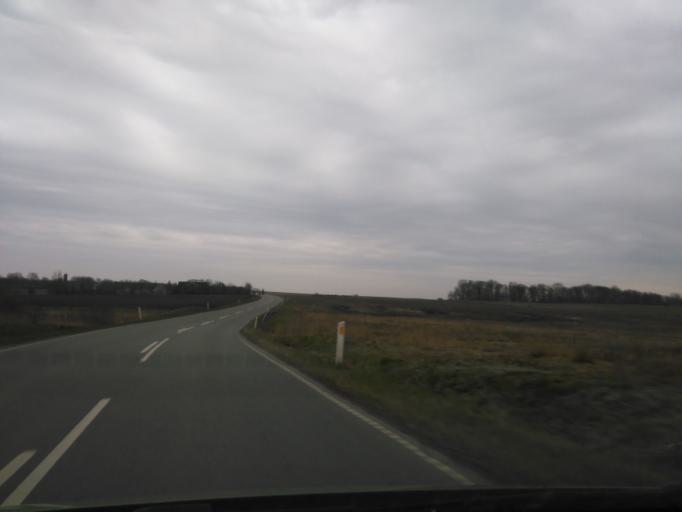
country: DK
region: Central Jutland
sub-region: Randers Kommune
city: Spentrup
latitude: 56.5304
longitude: 10.0001
